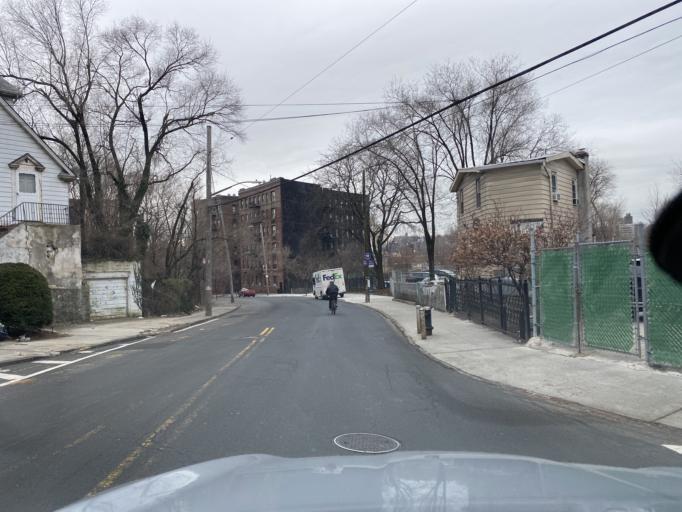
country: US
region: New York
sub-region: New York County
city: Inwood
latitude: 40.8788
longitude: -73.8996
